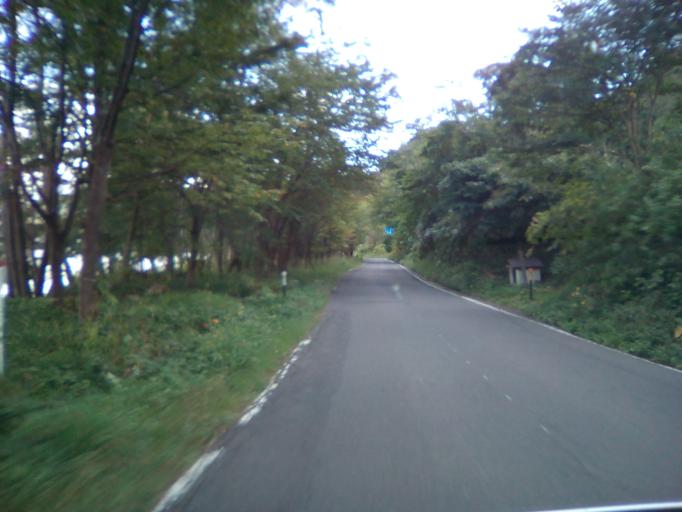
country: JP
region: Hokkaido
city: Date
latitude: 42.5811
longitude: 140.7959
